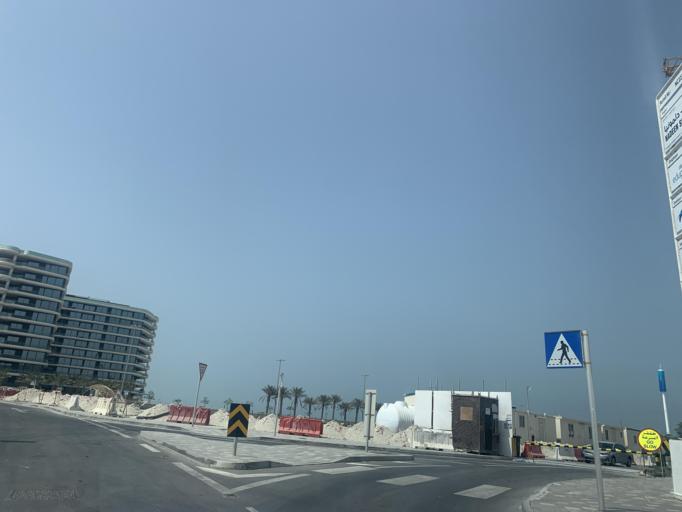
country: BH
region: Muharraq
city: Al Hadd
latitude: 26.2726
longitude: 50.6732
